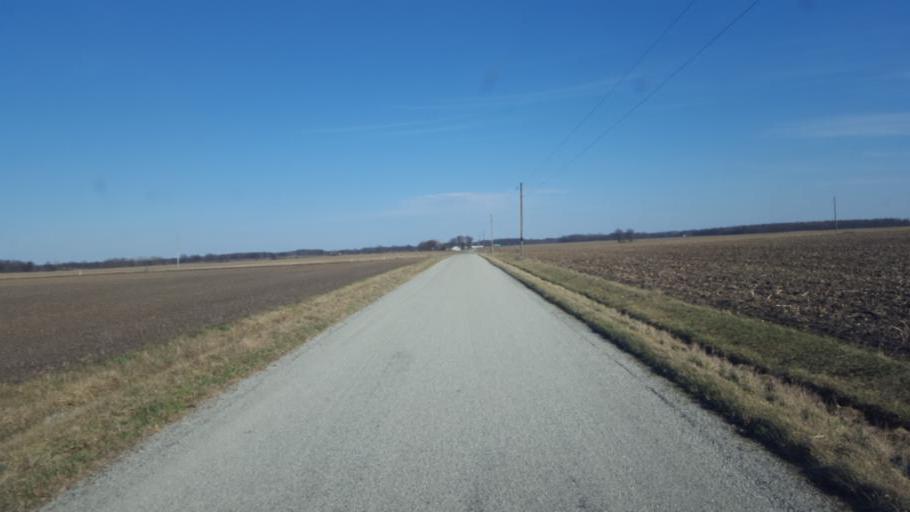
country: US
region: Ohio
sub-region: Crawford County
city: Bucyrus
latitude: 40.7034
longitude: -82.9791
